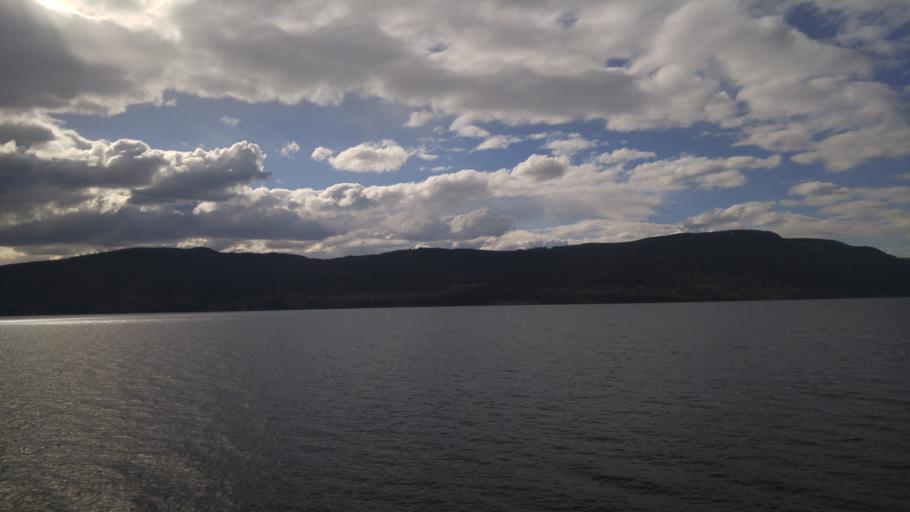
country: NO
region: Hedmark
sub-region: Stange
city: Stange
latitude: 60.5376
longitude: 11.2429
